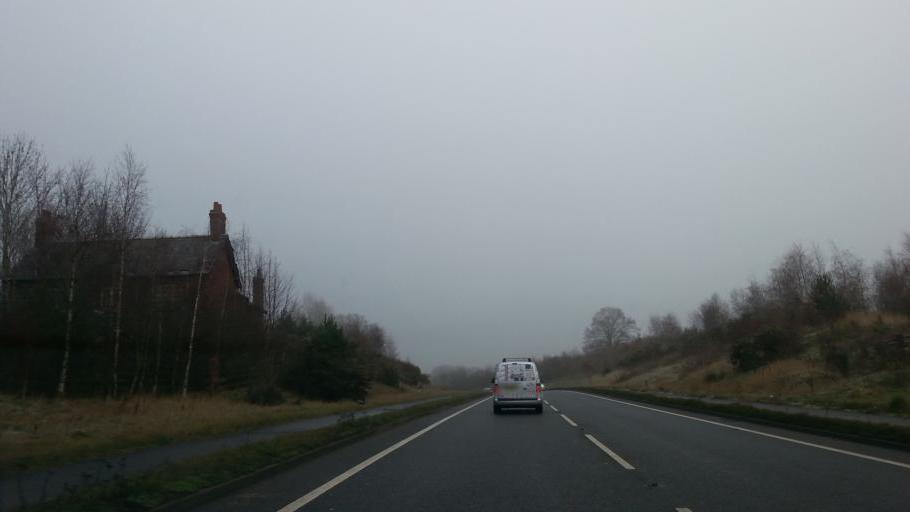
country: GB
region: England
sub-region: Cheshire East
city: Alderley Edge
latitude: 53.3082
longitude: -2.2429
